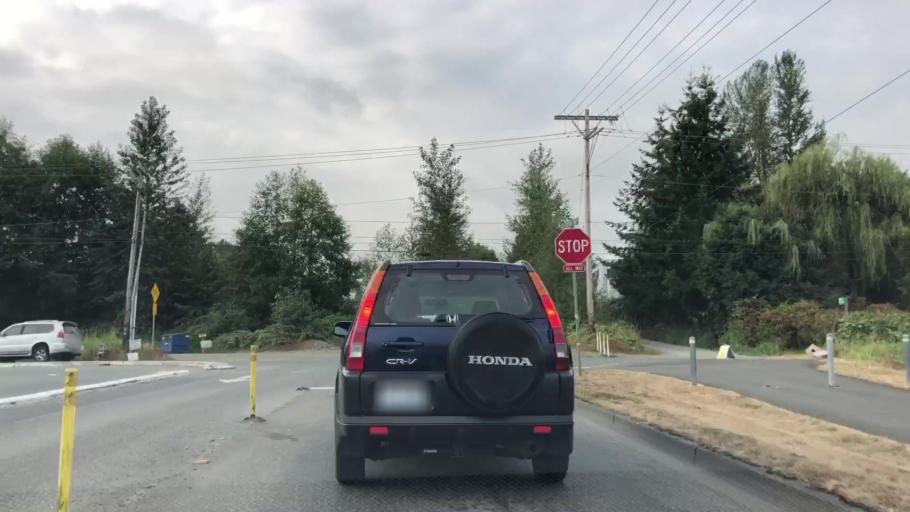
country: US
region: Washington
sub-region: Snohomish County
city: Monroe
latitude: 47.8491
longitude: -122.0122
